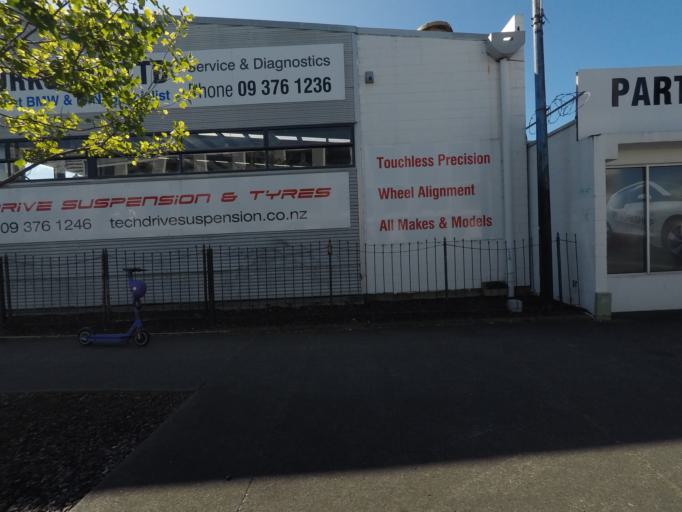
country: NZ
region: Auckland
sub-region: Auckland
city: Auckland
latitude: -36.8654
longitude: 174.7441
